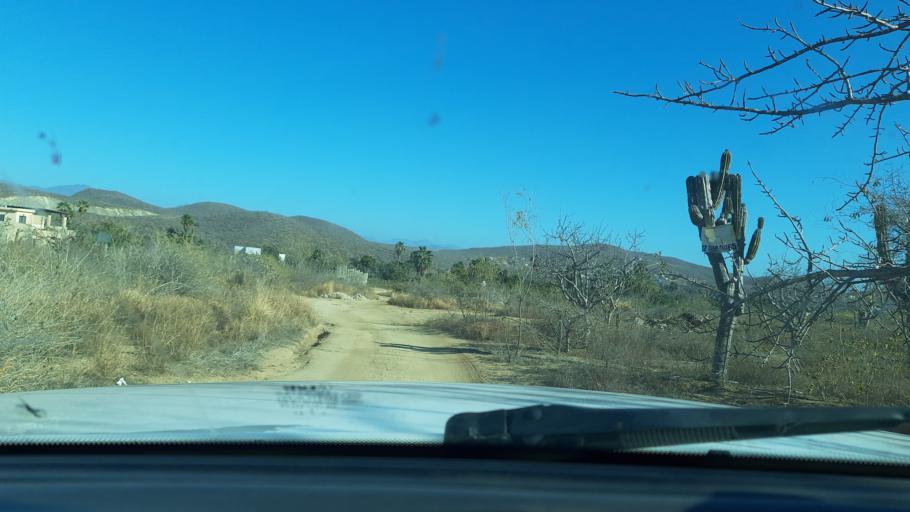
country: MX
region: Baja California Sur
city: Todos Santos
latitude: 23.4728
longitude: -110.2205
